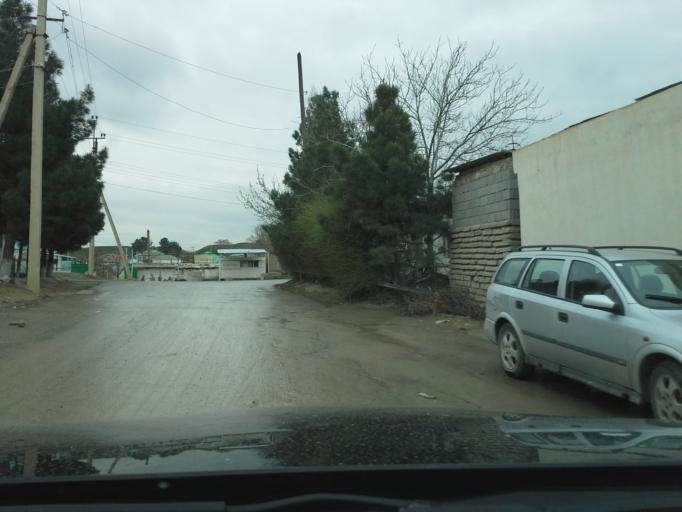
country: TM
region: Ahal
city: Abadan
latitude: 37.9557
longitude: 58.2065
